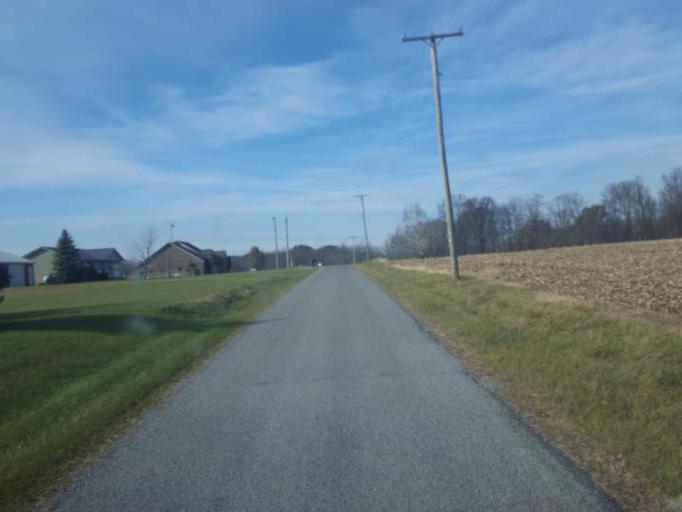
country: US
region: Ohio
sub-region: Crawford County
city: Crestline
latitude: 40.8504
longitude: -82.7867
